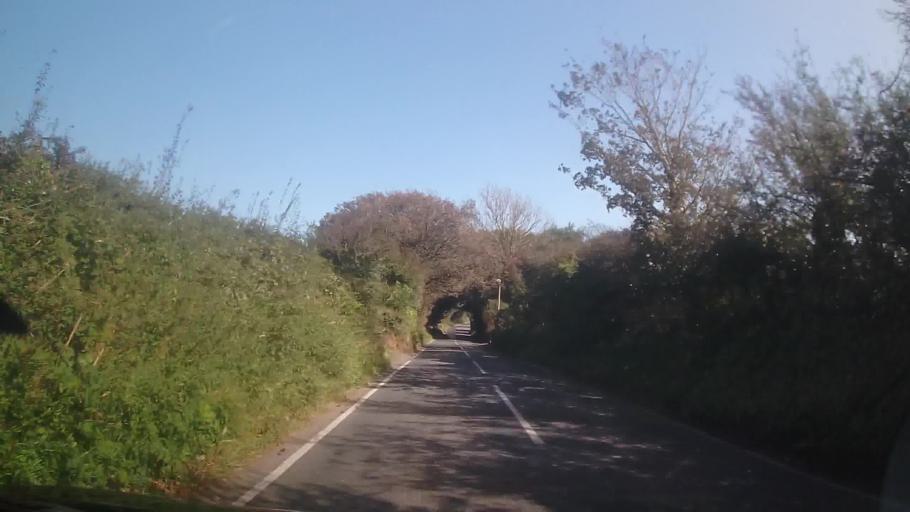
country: GB
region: Wales
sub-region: Pembrokeshire
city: Mathry
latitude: 51.9431
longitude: -5.0552
